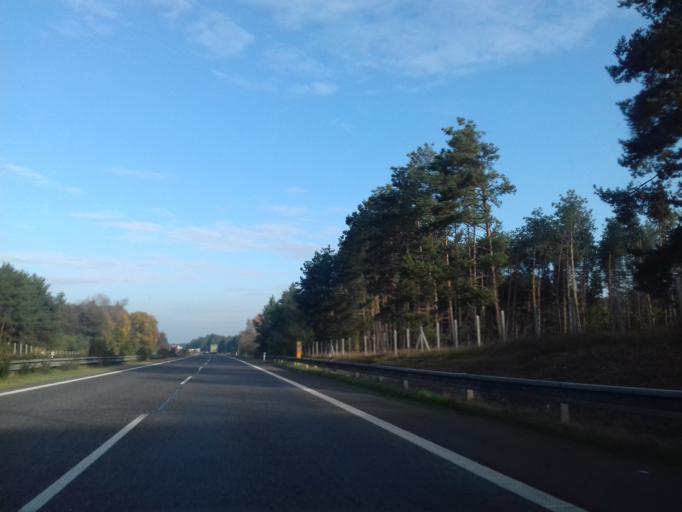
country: SK
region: Bratislavsky
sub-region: Okres Malacky
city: Malacky
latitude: 48.4425
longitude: 17.0430
